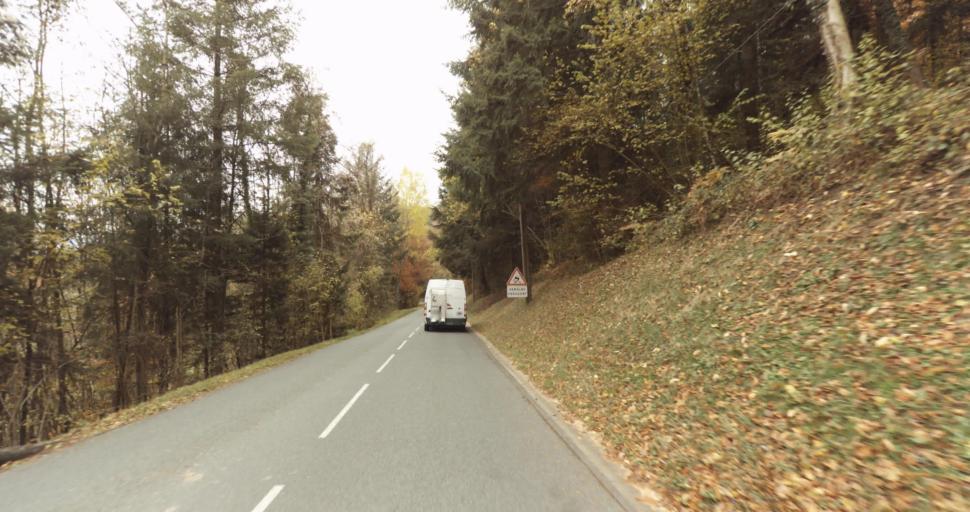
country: FR
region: Rhone-Alpes
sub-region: Departement de la Haute-Savoie
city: Saint-Martin-Bellevue
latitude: 45.9683
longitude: 6.1533
